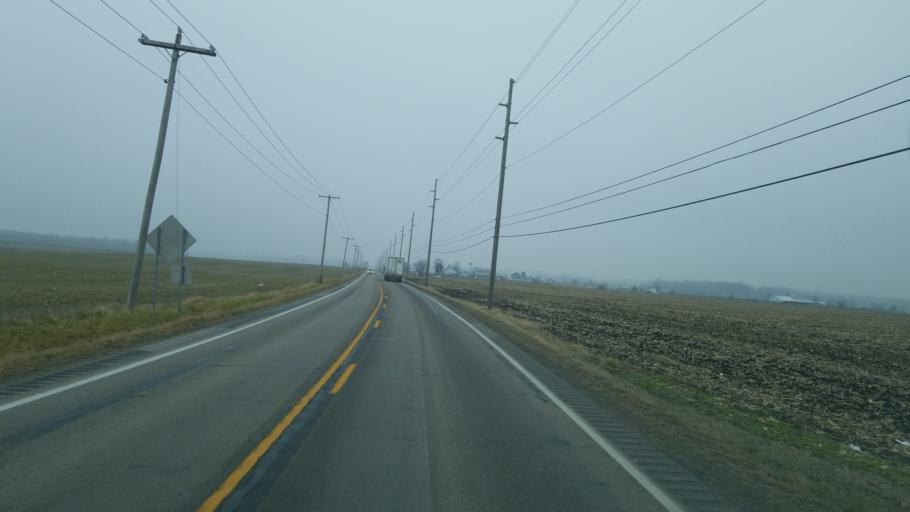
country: US
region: Indiana
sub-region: Adams County
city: Geneva
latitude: 40.5480
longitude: -84.9618
